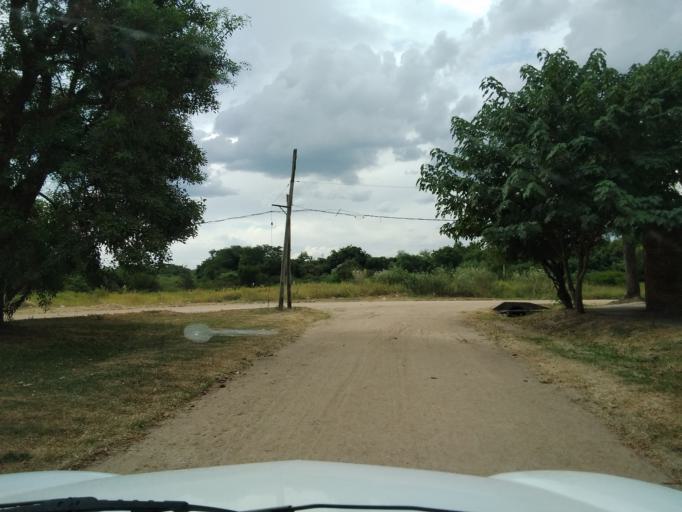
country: AR
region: Corrientes
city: Corrientes
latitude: -27.5182
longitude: -58.7928
